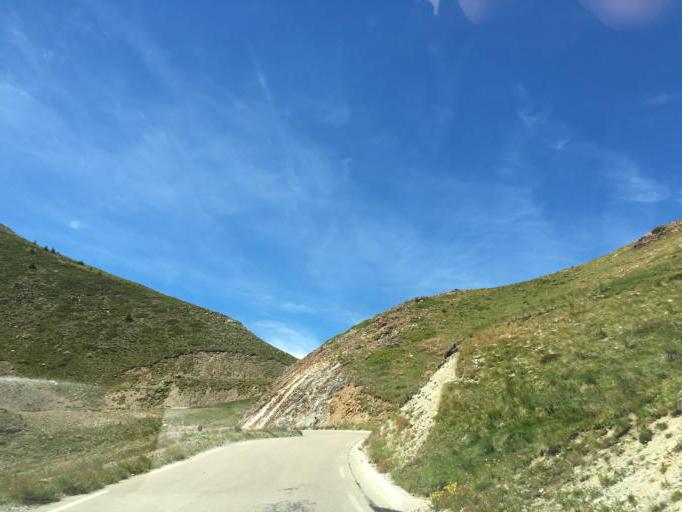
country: IT
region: Piedmont
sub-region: Provincia di Cuneo
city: Vinadio
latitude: 44.2019
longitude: 7.1523
